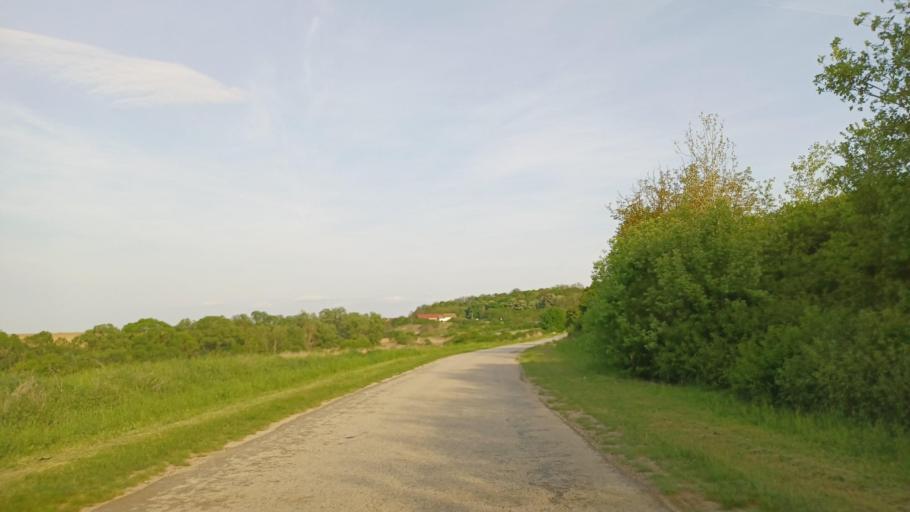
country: HU
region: Baranya
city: Kozarmisleny
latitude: 45.9631
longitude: 18.3743
